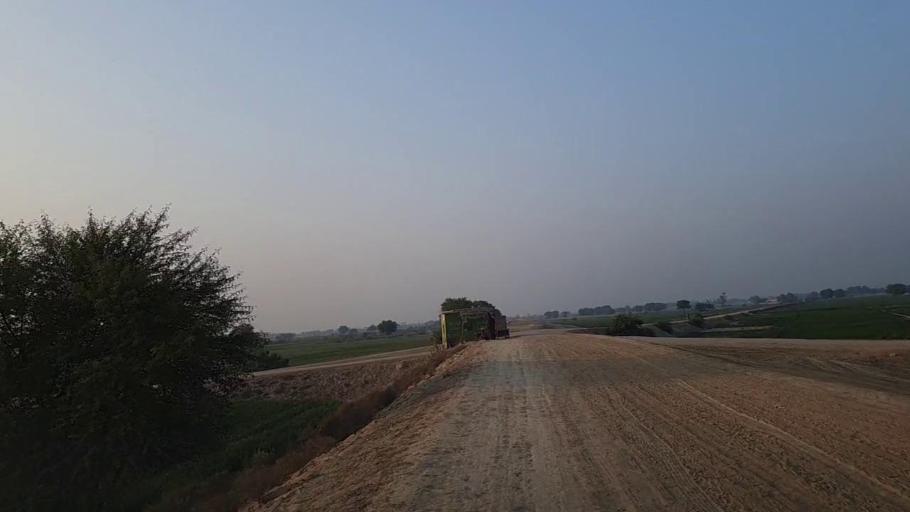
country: PK
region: Sindh
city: Sann
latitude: 26.1943
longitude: 68.0895
